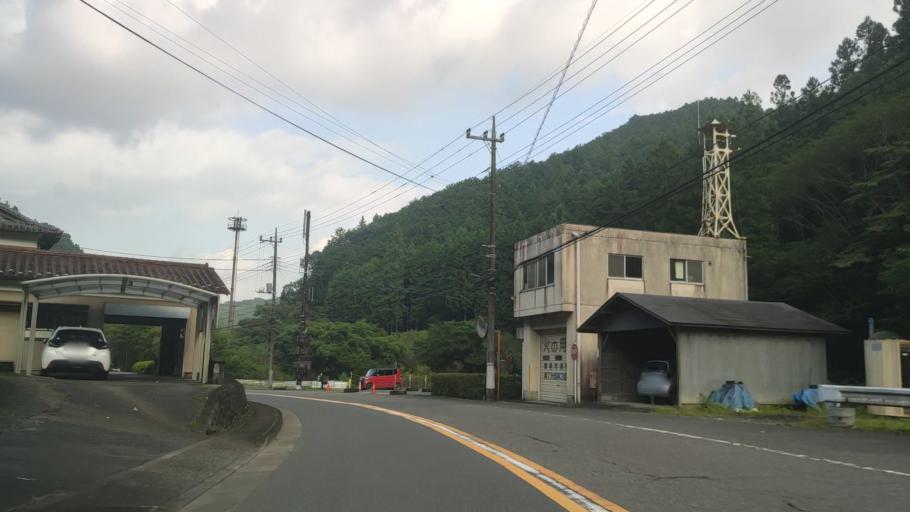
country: JP
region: Tokyo
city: Ome
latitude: 35.8331
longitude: 139.2223
